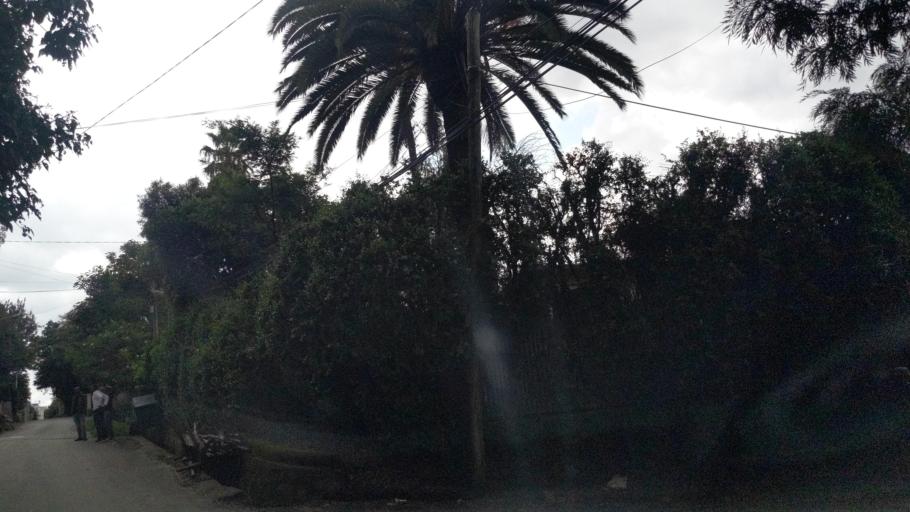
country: ET
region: Adis Abeba
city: Addis Ababa
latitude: 8.9971
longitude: 38.7802
